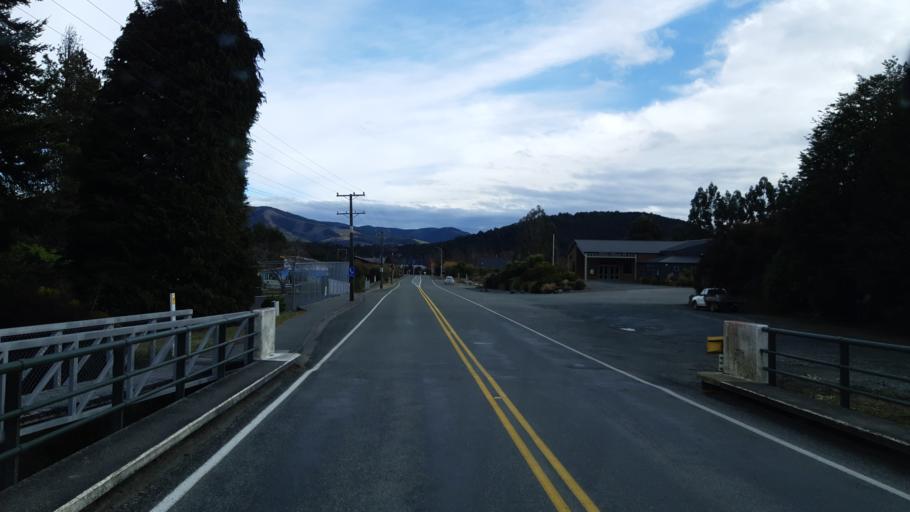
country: NZ
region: Tasman
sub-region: Tasman District
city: Wakefield
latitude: -41.8011
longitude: 172.8532
